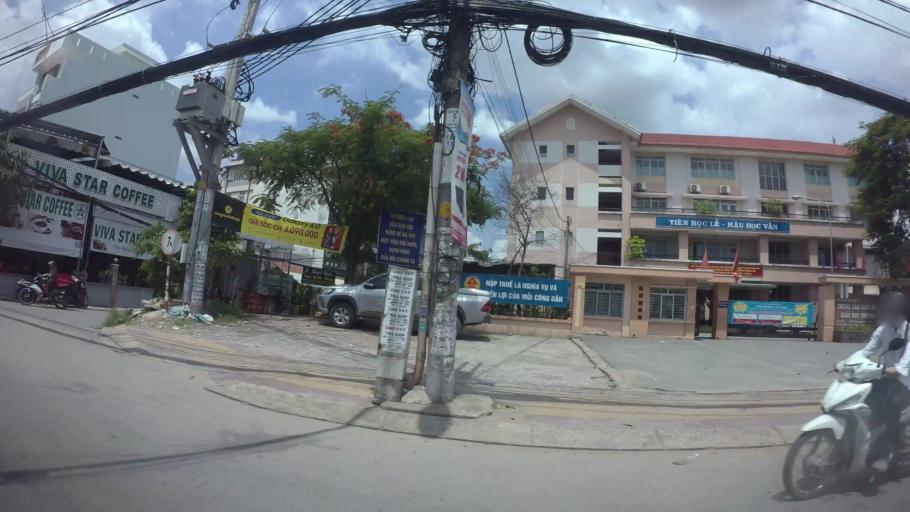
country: VN
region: Ho Chi Minh City
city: Quan Chin
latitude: 10.8388
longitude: 106.7805
